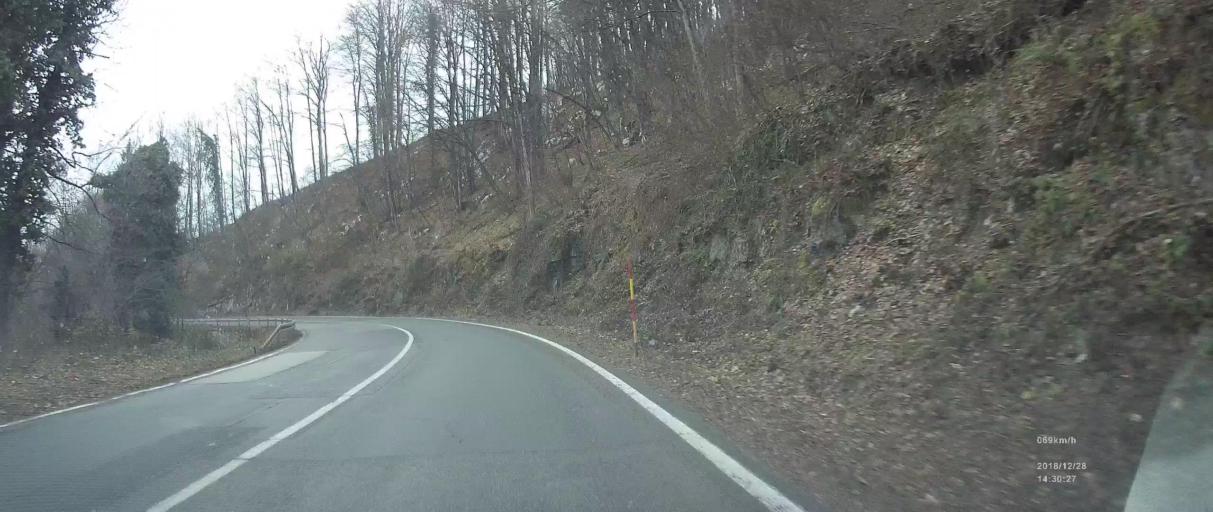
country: HR
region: Primorsko-Goranska
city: Vrbovsko
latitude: 45.4181
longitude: 15.1293
